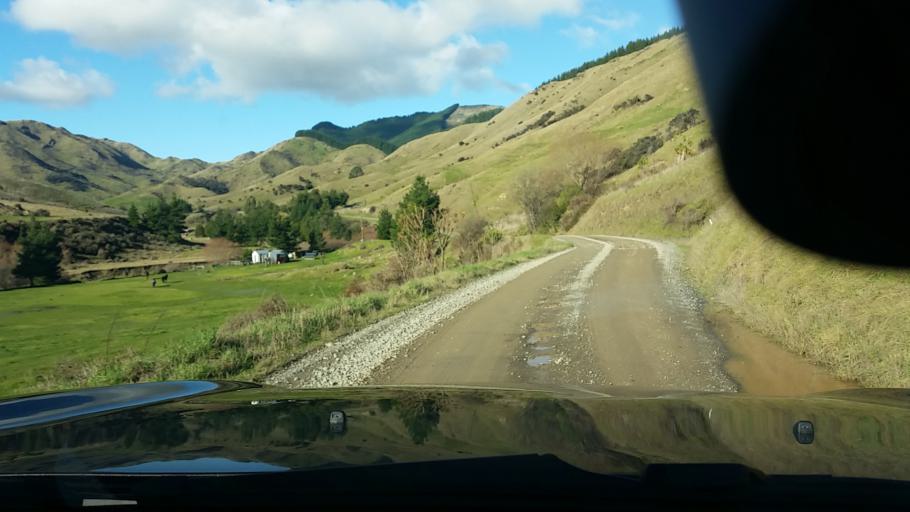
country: NZ
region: Marlborough
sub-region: Marlborough District
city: Blenheim
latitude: -41.6027
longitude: 173.9571
